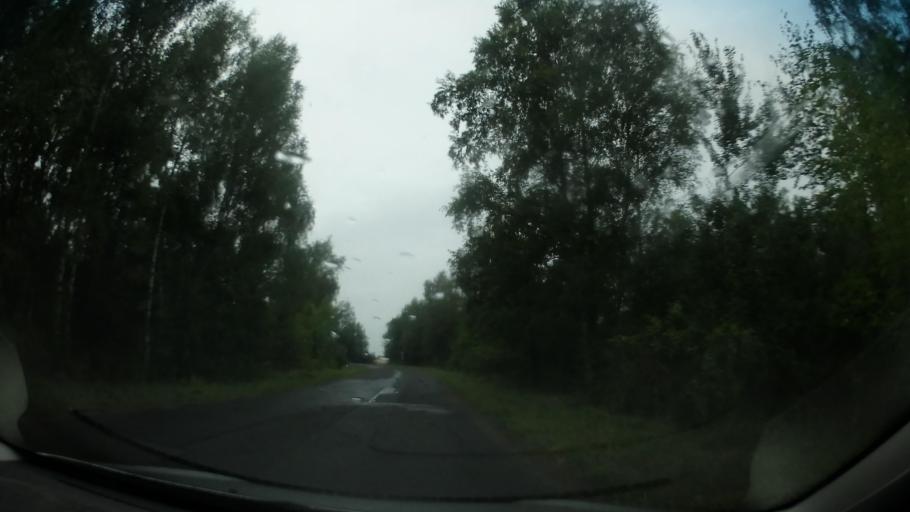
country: CZ
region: Central Bohemia
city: Milovice
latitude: 50.2429
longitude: 14.8985
